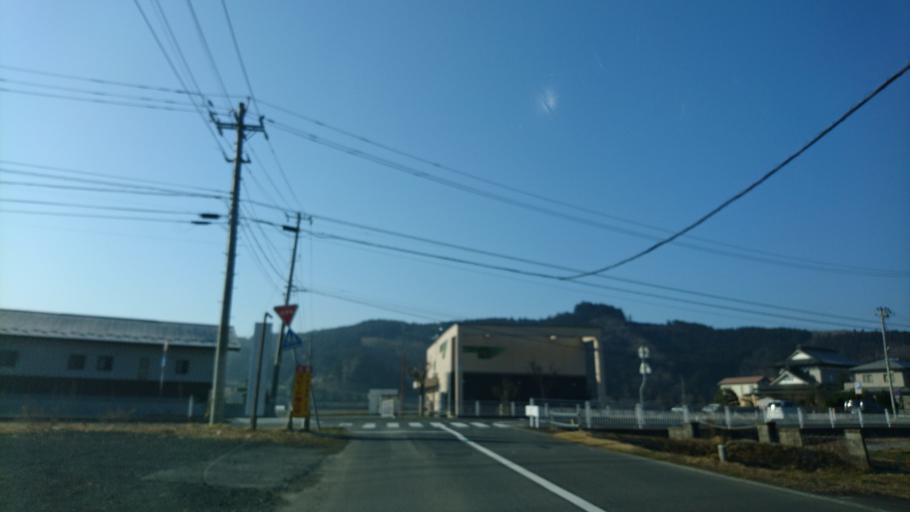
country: JP
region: Iwate
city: Ichinoseki
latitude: 38.9002
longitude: 141.2792
